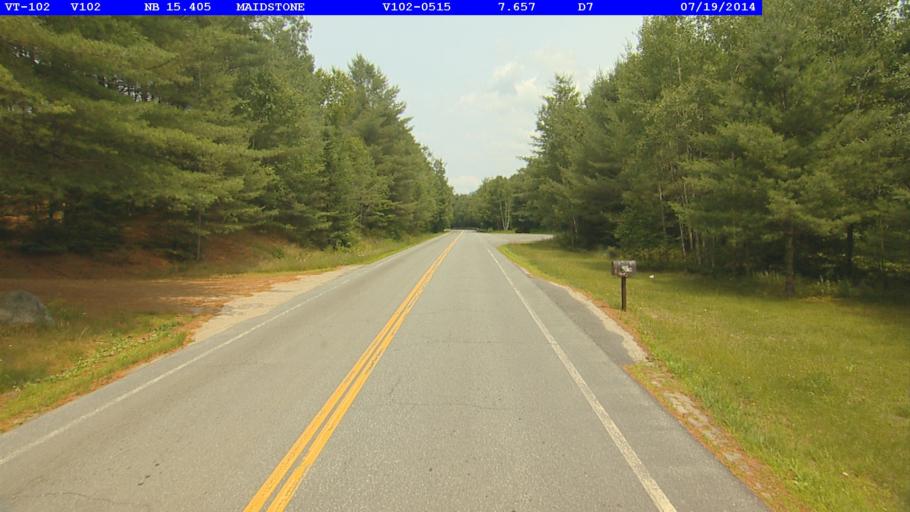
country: US
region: New Hampshire
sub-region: Coos County
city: Stratford
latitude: 44.6602
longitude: -71.5910
